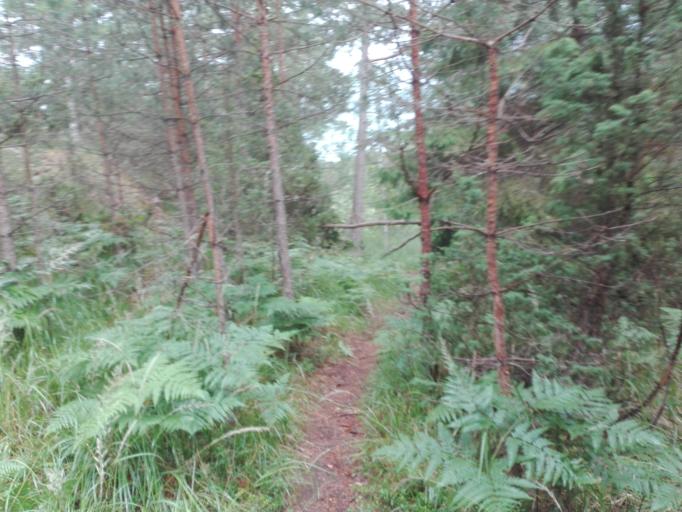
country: SE
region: Stockholm
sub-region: Nacka Kommun
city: Fisksatra
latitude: 59.2791
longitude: 18.2486
